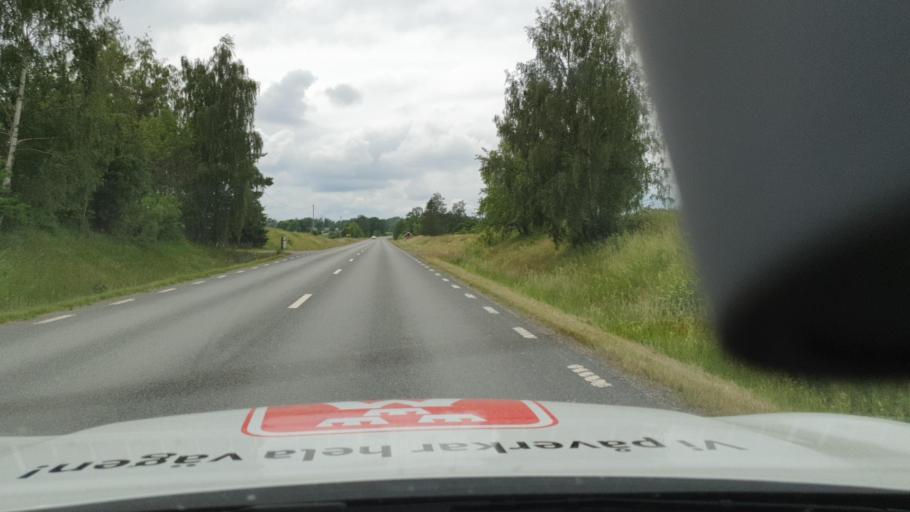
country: SE
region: Vaestra Goetaland
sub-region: Hjo Kommun
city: Hjo
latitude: 58.2265
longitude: 14.1954
